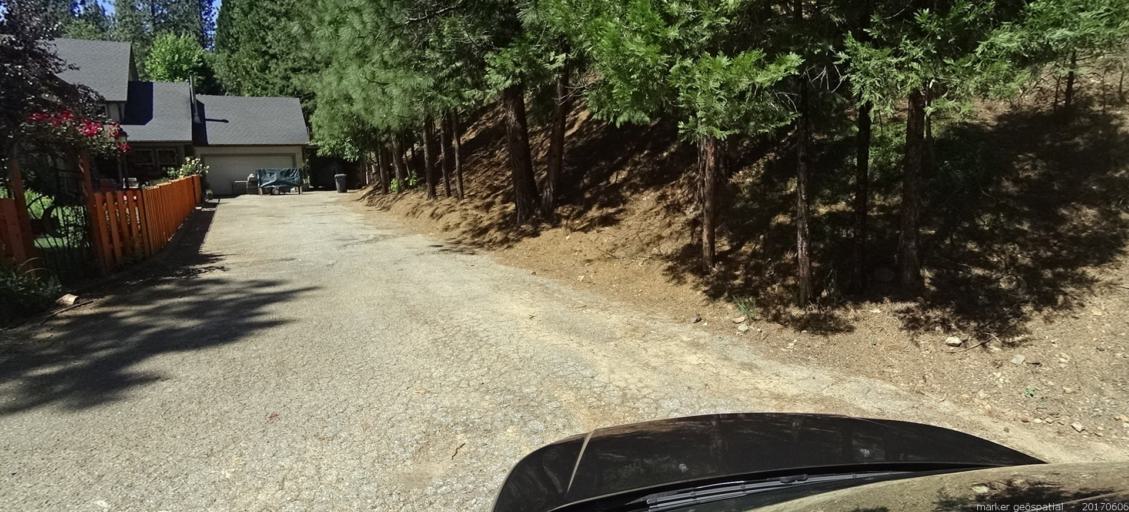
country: US
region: California
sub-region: Siskiyou County
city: Dunsmuir
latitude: 41.2143
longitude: -122.2751
